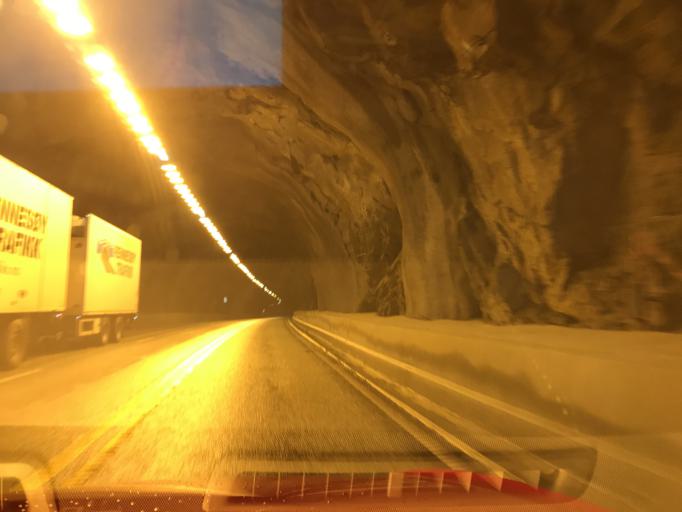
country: NO
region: Rogaland
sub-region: Rennesoy
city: Vikevag
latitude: 59.0721
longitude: 5.6773
